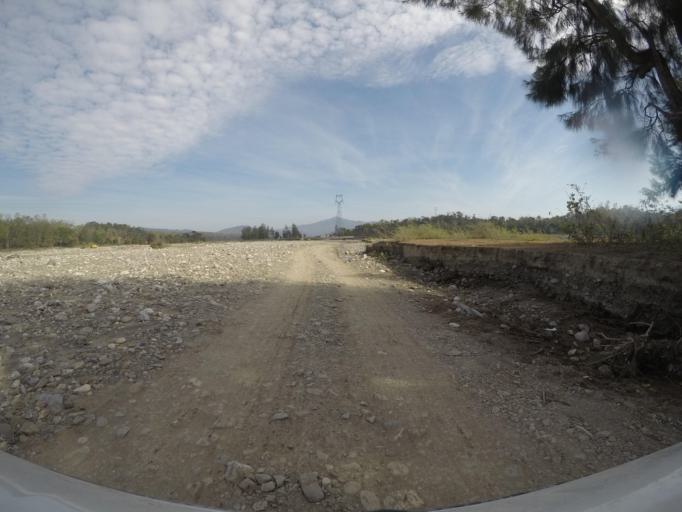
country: TL
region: Bobonaro
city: Maliana
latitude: -8.9075
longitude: 125.2129
